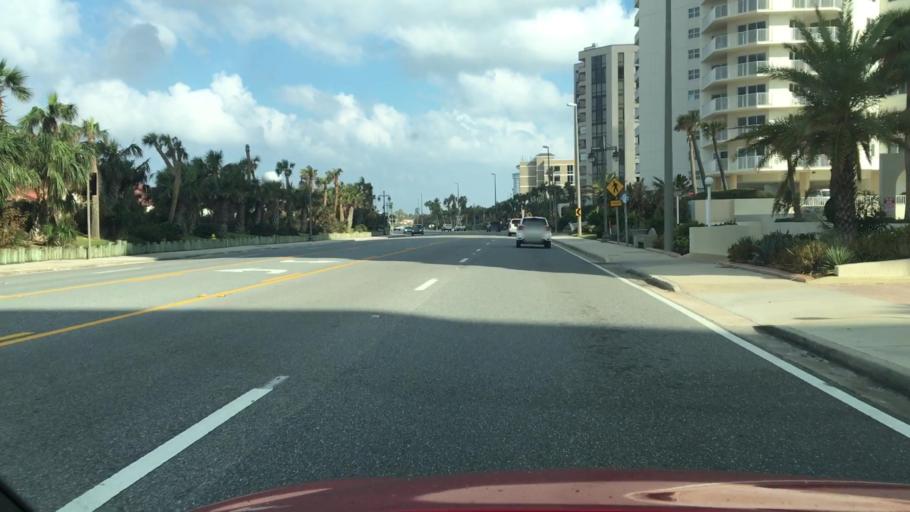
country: US
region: Florida
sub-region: Volusia County
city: Daytona Beach Shores
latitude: 29.1706
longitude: -80.9795
